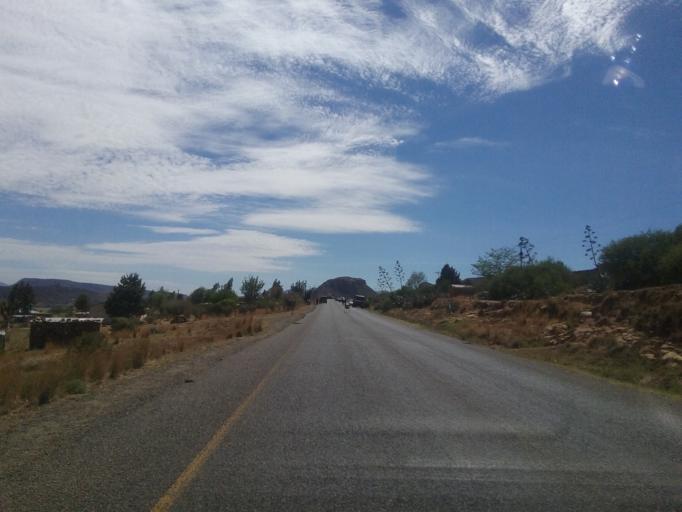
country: LS
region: Mohale's Hoek District
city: Mohale's Hoek
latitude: -30.1830
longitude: 27.4254
